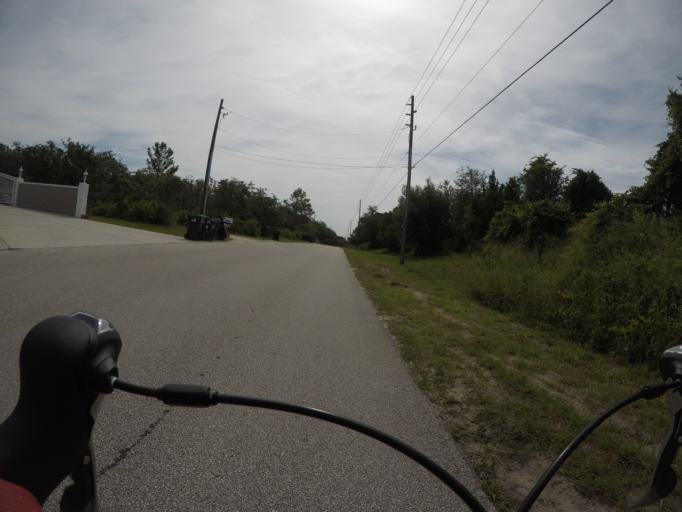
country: US
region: Florida
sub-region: Osceola County
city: Buenaventura Lakes
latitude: 28.3782
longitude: -81.2334
